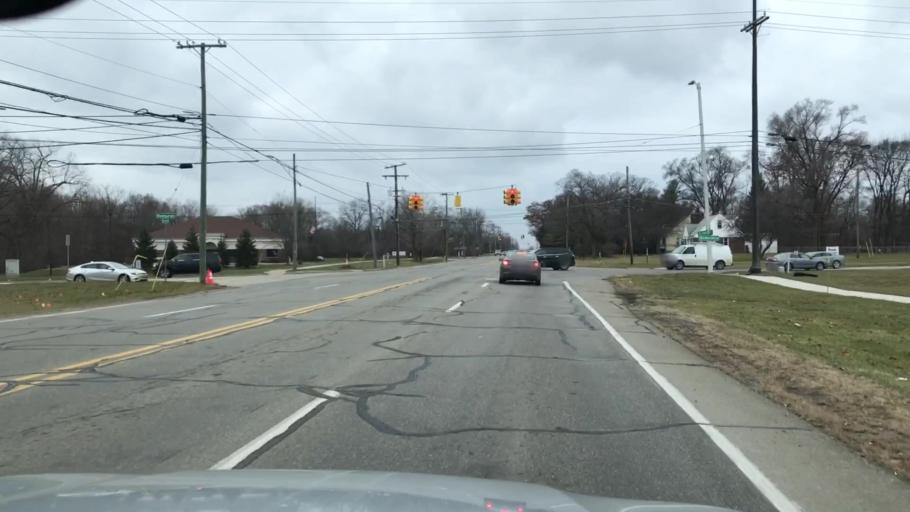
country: US
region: Michigan
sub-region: Wayne County
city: Westland
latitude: 42.3682
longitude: -83.4106
